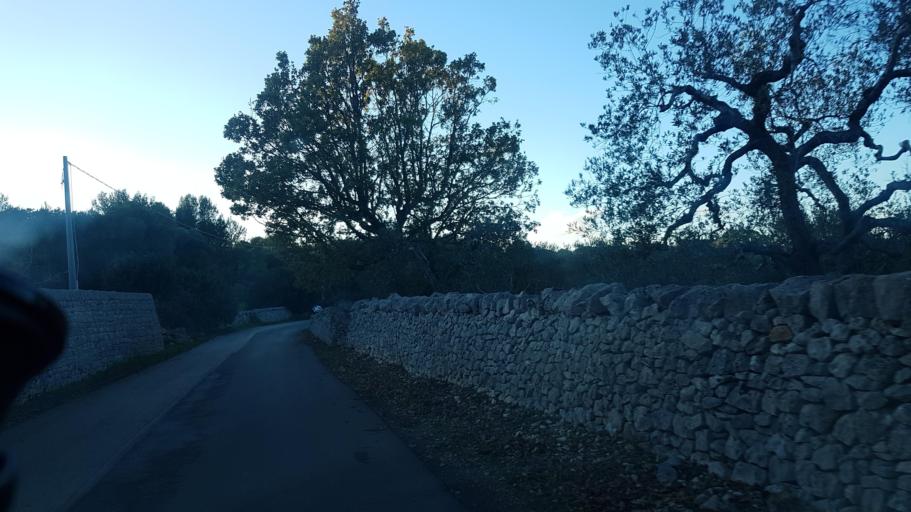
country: IT
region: Apulia
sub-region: Provincia di Brindisi
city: Ostuni
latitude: 40.7033
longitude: 17.5384
